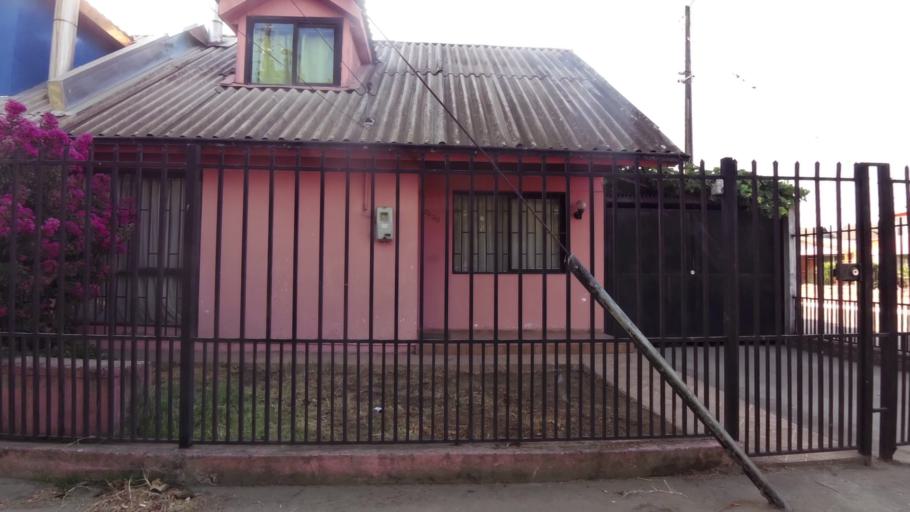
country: CL
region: Maule
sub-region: Provincia de Talca
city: Talca
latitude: -35.4120
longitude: -71.6534
